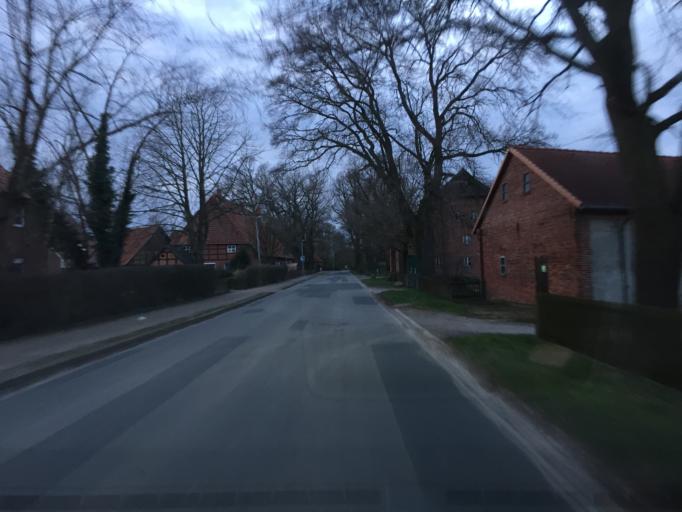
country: DE
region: Lower Saxony
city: Steimbke
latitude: 52.5960
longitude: 9.3976
